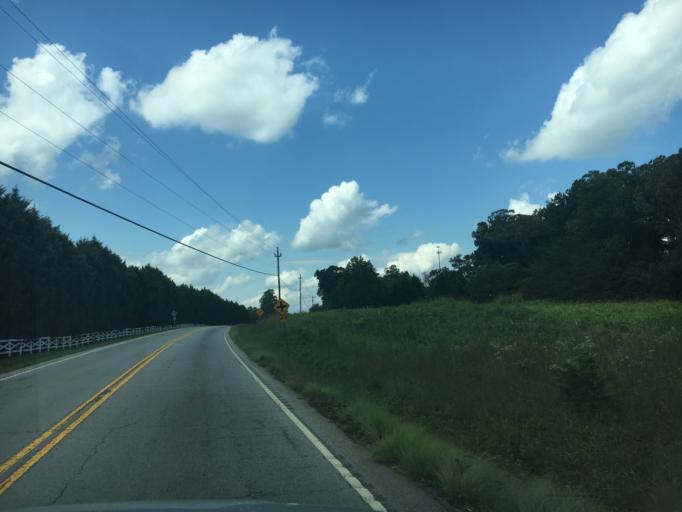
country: US
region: South Carolina
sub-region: Greenville County
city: Berea
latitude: 34.8877
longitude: -82.5225
